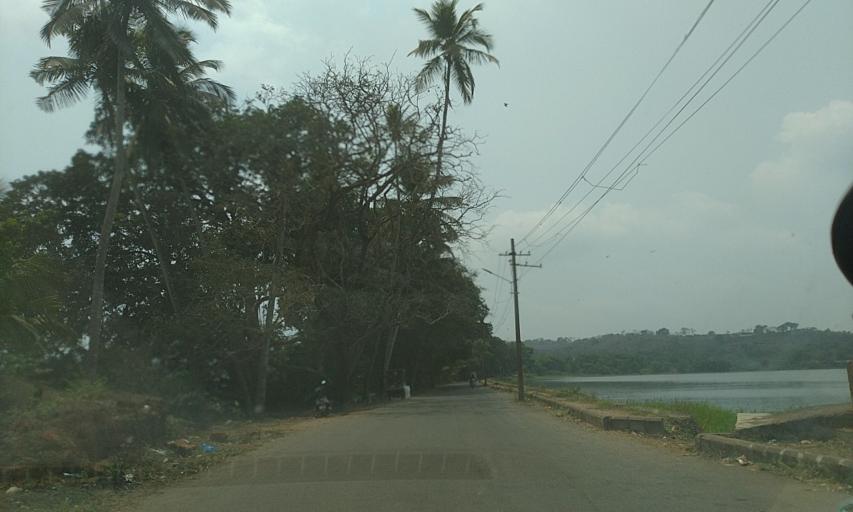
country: IN
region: Goa
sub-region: North Goa
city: Jua
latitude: 15.4861
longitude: 73.9301
